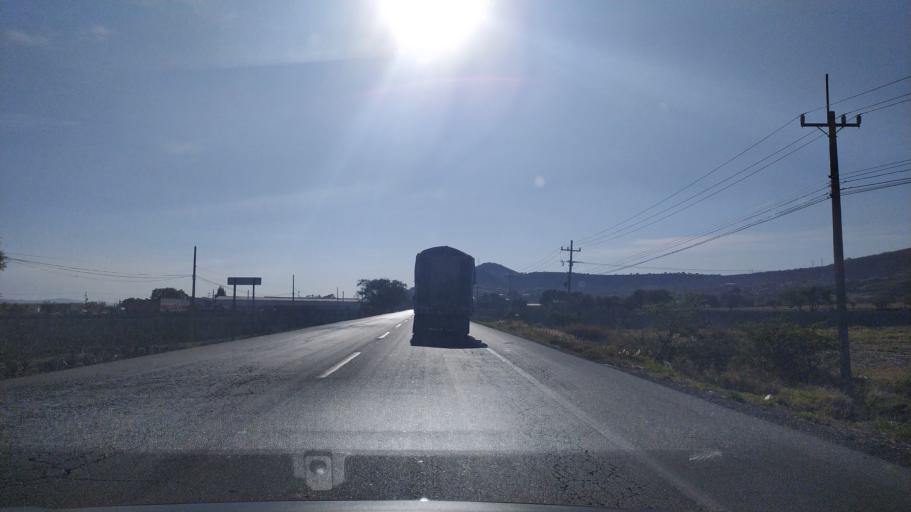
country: MX
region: Jalisco
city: Jamay
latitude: 20.2945
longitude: -102.6910
